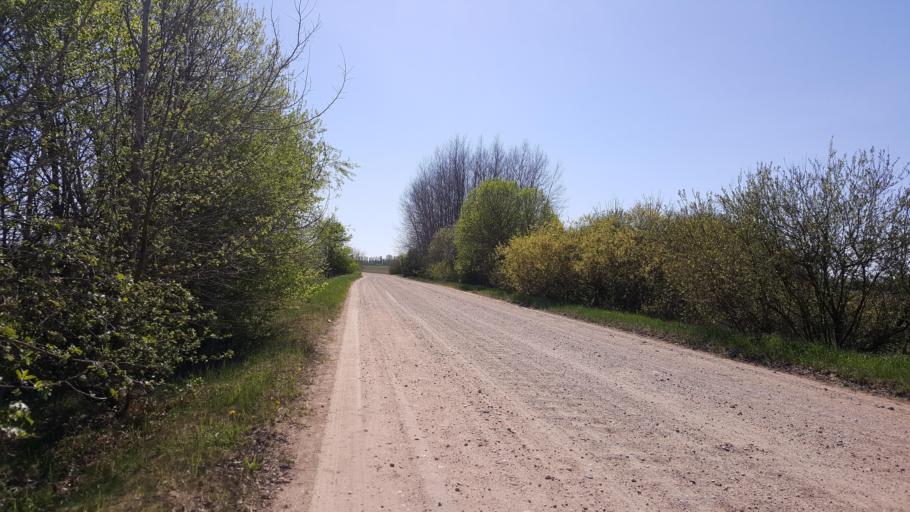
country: BY
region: Brest
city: Kamyanyets
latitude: 52.4502
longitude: 23.8681
